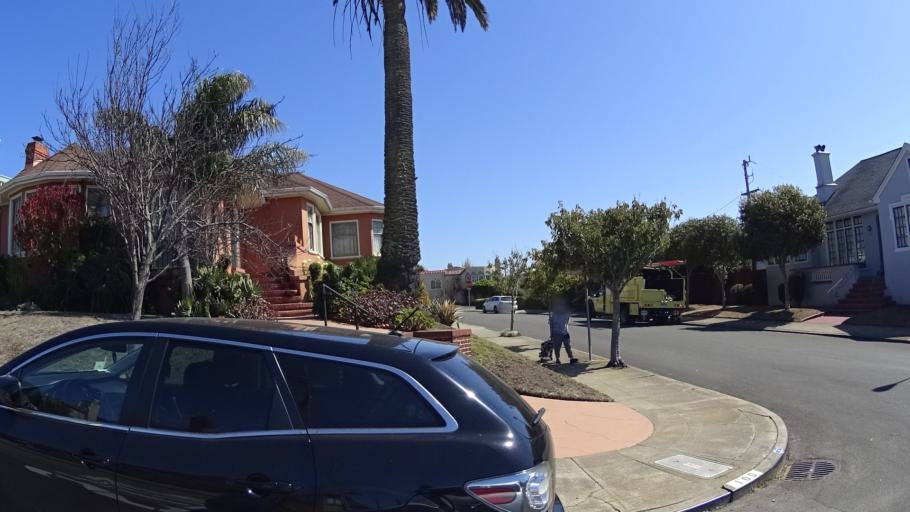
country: US
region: California
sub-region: San Mateo County
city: Daly City
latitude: 37.7302
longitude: -122.4550
